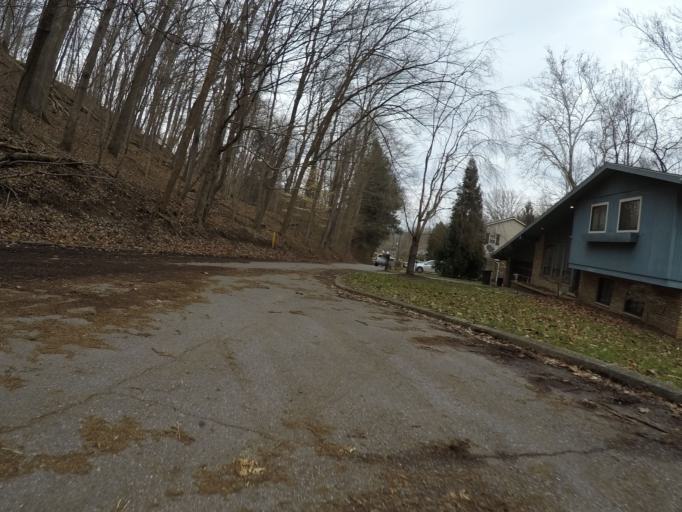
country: US
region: West Virginia
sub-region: Cabell County
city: Huntington
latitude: 38.3940
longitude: -82.4263
